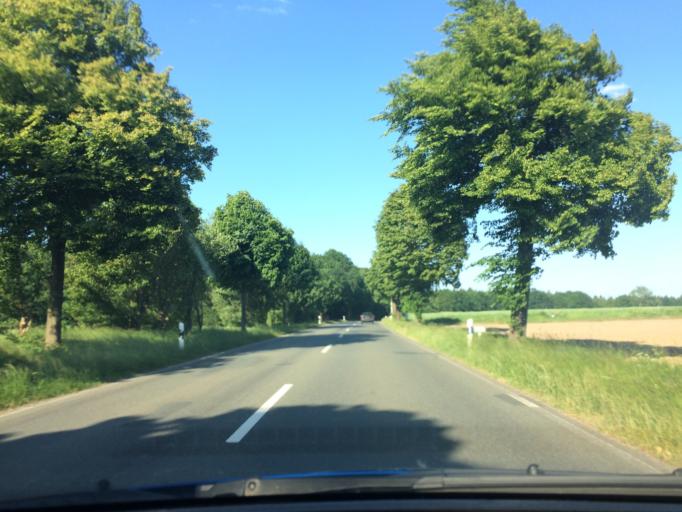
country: DE
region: Lower Saxony
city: Soltau
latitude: 53.0184
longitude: 9.8939
